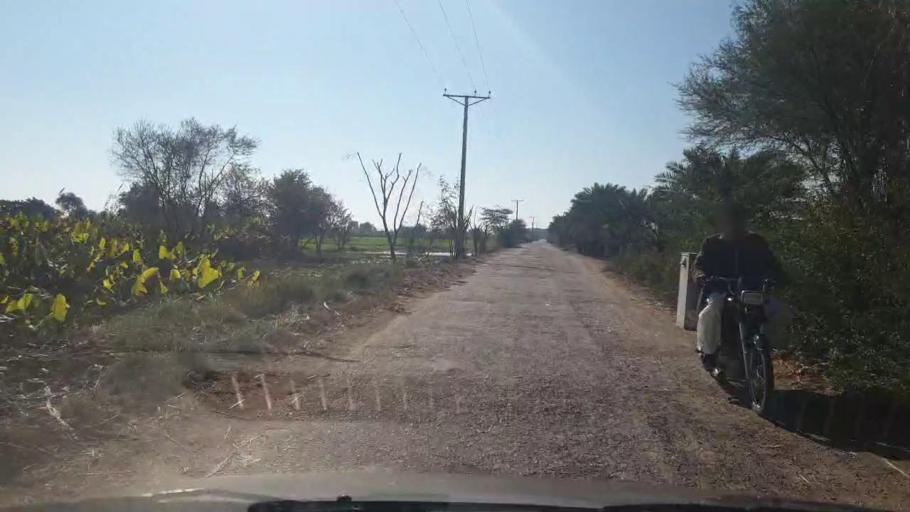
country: PK
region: Sindh
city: Bozdar
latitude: 27.2565
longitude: 68.6525
